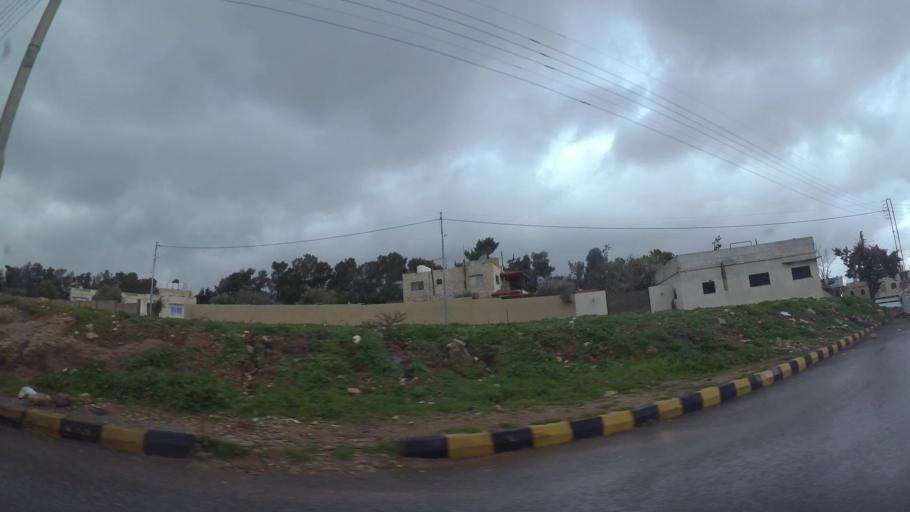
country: JO
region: Amman
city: Al Jubayhah
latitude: 32.0376
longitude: 35.8645
